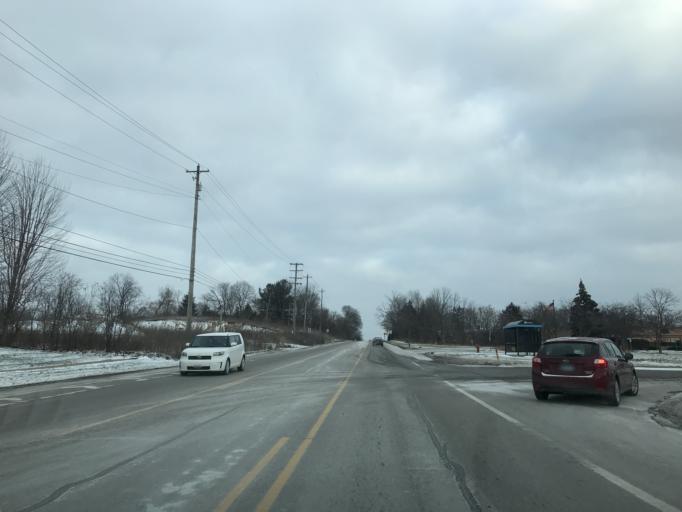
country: US
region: Michigan
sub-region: Washtenaw County
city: Ann Arbor
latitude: 42.2298
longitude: -83.7189
